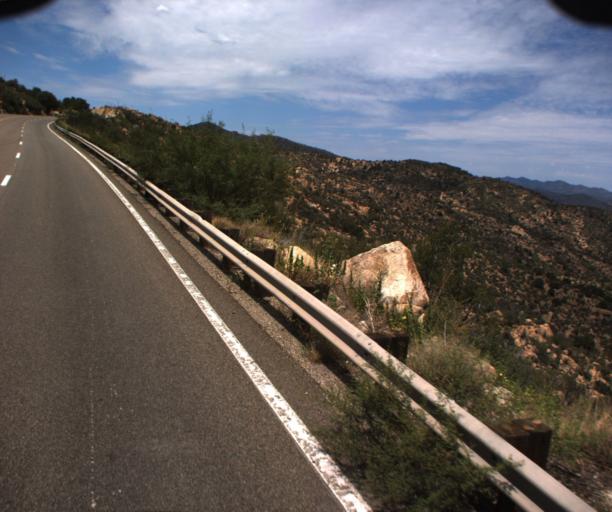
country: US
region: Arizona
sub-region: Gila County
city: Miami
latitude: 33.3662
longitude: -110.9670
